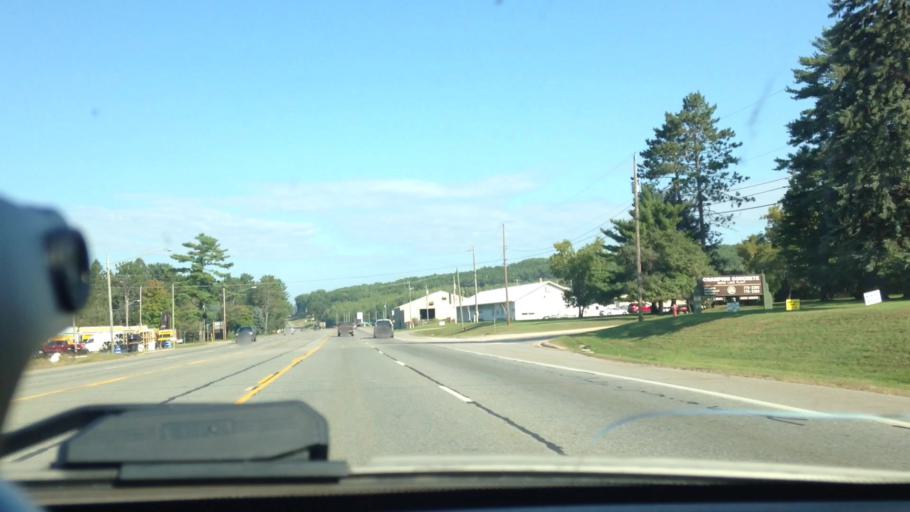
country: US
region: Michigan
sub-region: Dickinson County
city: Iron Mountain
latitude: 45.8477
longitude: -88.0507
